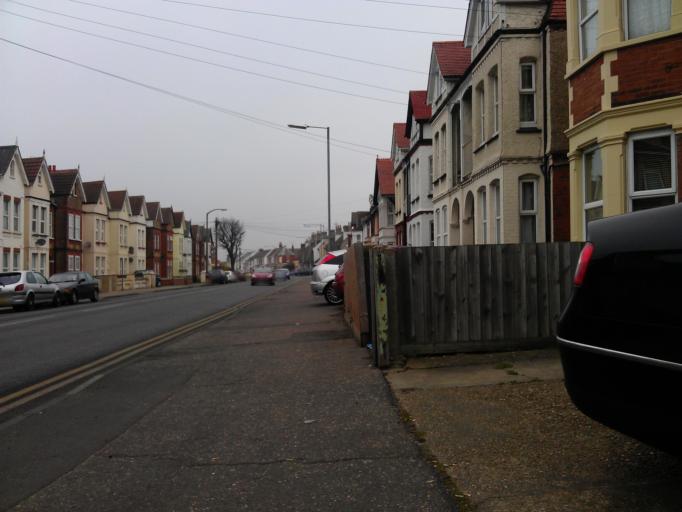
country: GB
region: England
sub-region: Essex
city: Clacton-on-Sea
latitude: 51.7957
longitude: 1.1525
